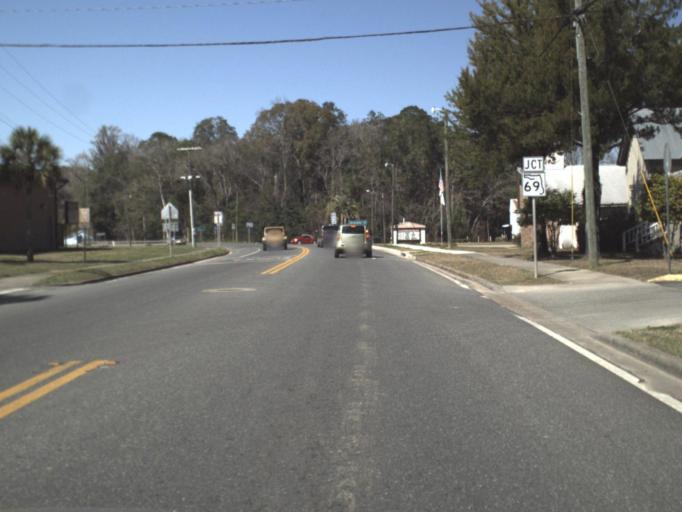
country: US
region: Florida
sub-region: Calhoun County
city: Blountstown
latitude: 30.4492
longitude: -85.0457
